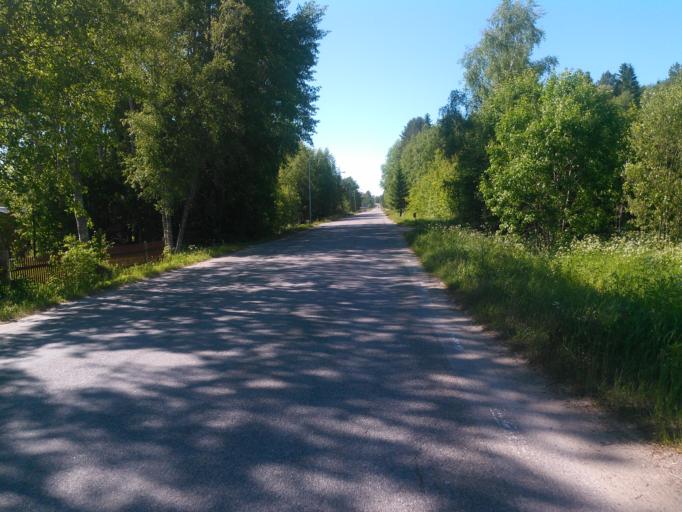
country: SE
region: Vaesterbotten
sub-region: Umea Kommun
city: Roback
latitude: 63.8216
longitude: 20.1905
